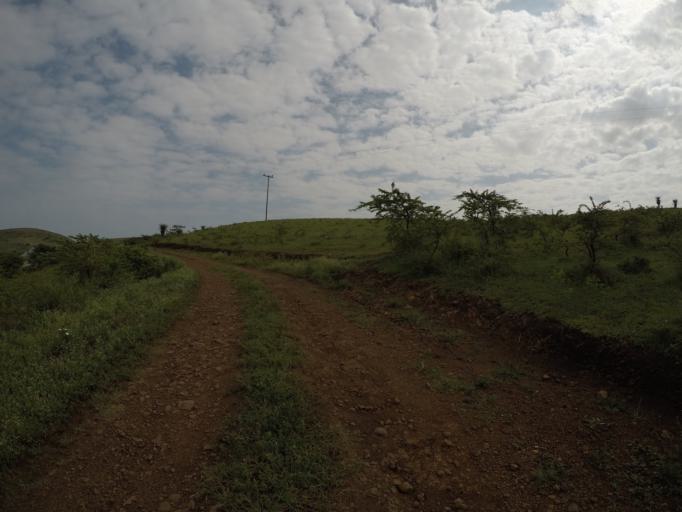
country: ZA
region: KwaZulu-Natal
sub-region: uThungulu District Municipality
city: Empangeni
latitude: -28.6256
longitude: 31.9017
